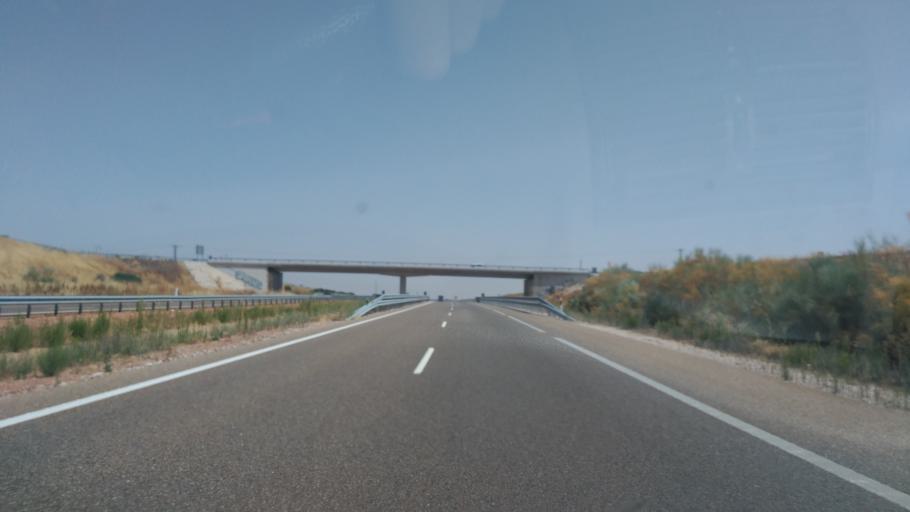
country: ES
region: Castille and Leon
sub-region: Provincia de Salamanca
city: Robliza de Cojos
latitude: 40.8749
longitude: -5.9821
